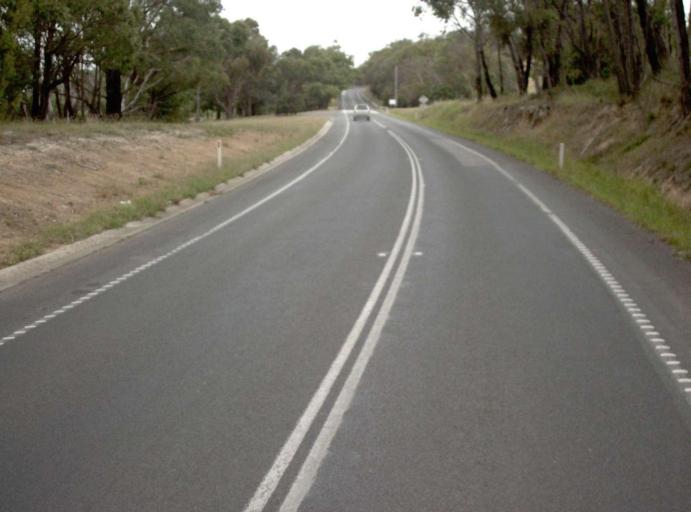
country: AU
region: Victoria
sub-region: Yarra Ranges
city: Yarra Glen
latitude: -37.5684
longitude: 145.4150
